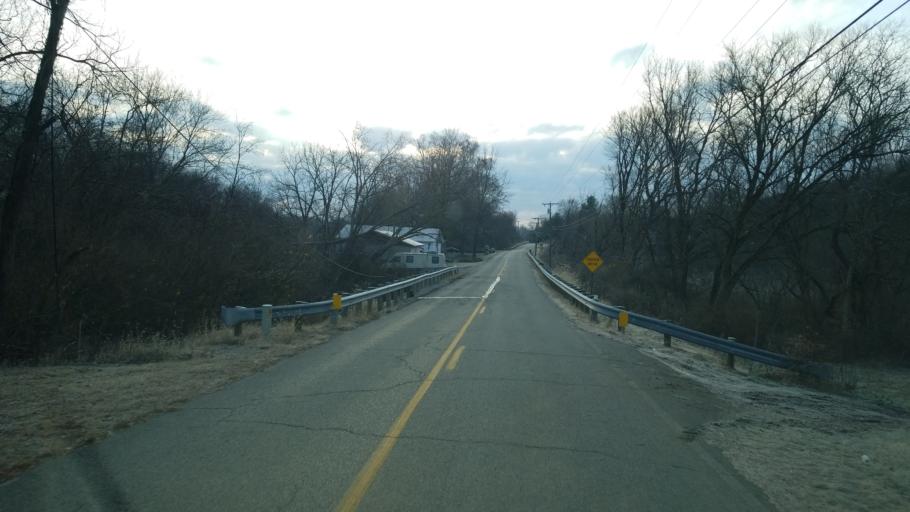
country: US
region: Ohio
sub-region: Ross County
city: Chillicothe
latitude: 39.2695
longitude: -82.9243
